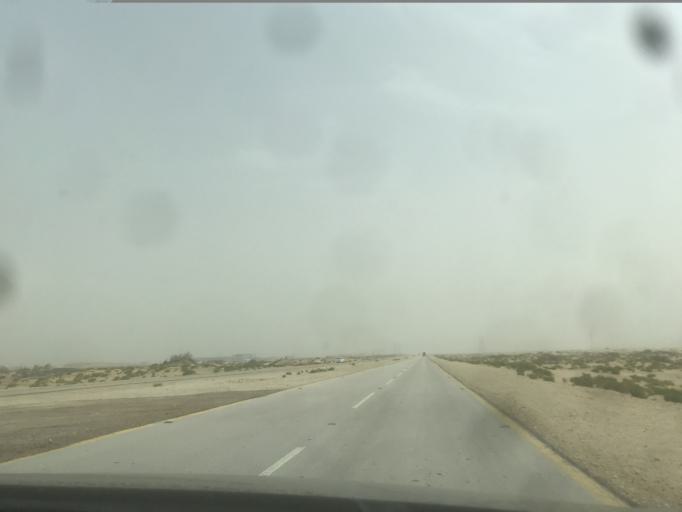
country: SA
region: Eastern Province
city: Abqaiq
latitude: 25.9091
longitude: 49.9360
